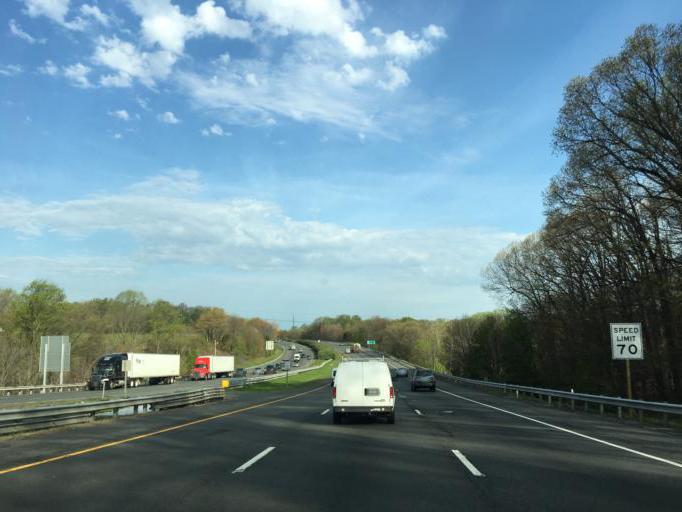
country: US
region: Maryland
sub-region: Carroll County
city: Mount Airy
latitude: 39.3614
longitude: -77.1769
